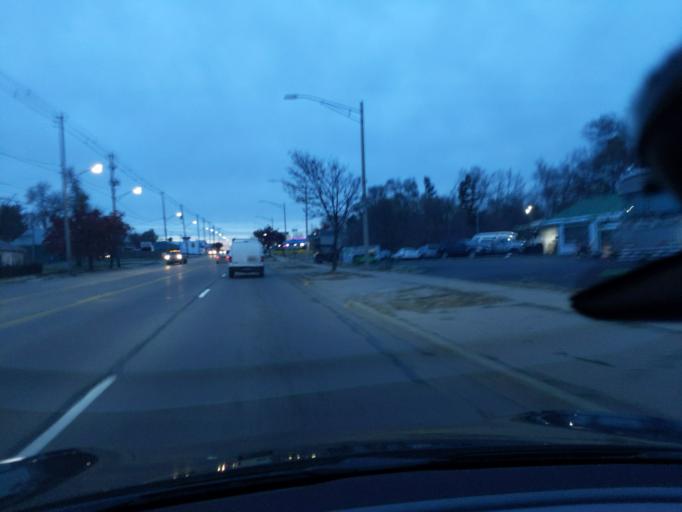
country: US
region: Michigan
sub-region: Ingham County
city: Lansing
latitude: 42.6987
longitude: -84.5480
